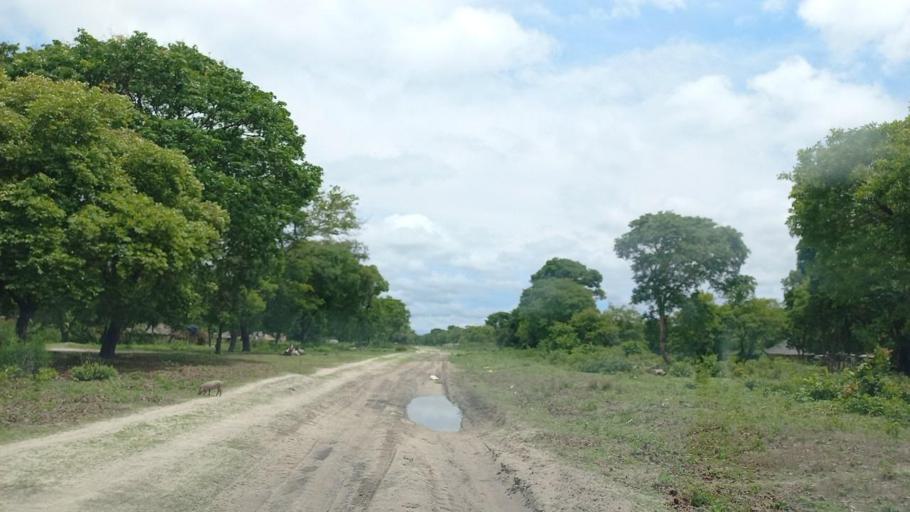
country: ZM
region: North-Western
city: Kabompo
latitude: -13.1879
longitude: 23.9574
